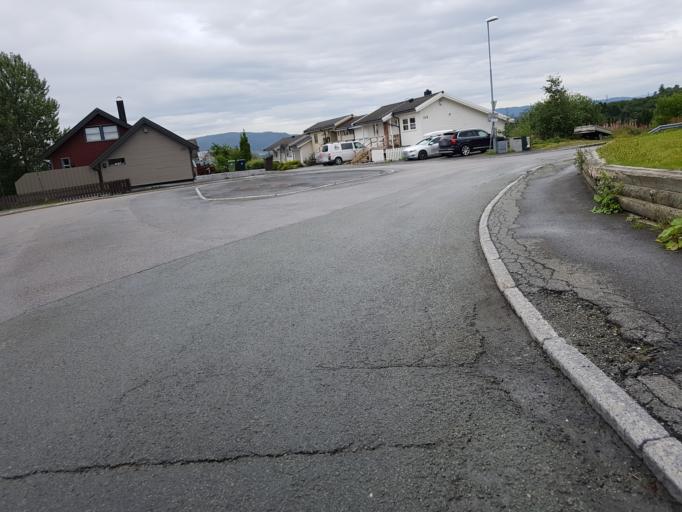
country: NO
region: Sor-Trondelag
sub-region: Trondheim
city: Trondheim
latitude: 63.3853
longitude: 10.3429
